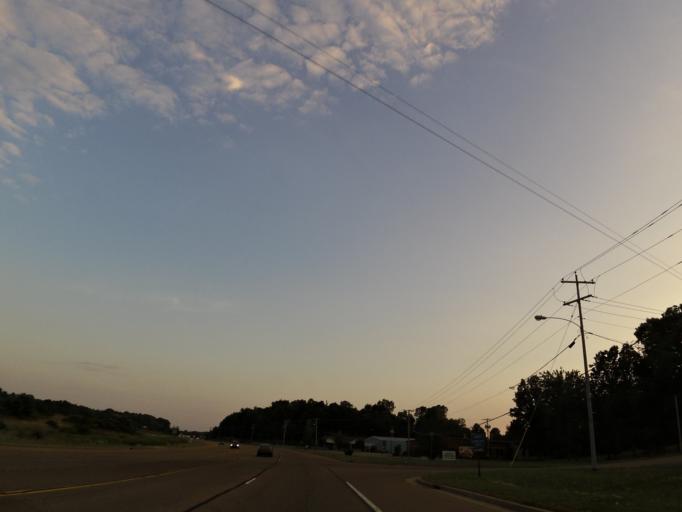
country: US
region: Tennessee
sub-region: Henry County
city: Paris
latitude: 36.2885
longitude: -88.3214
